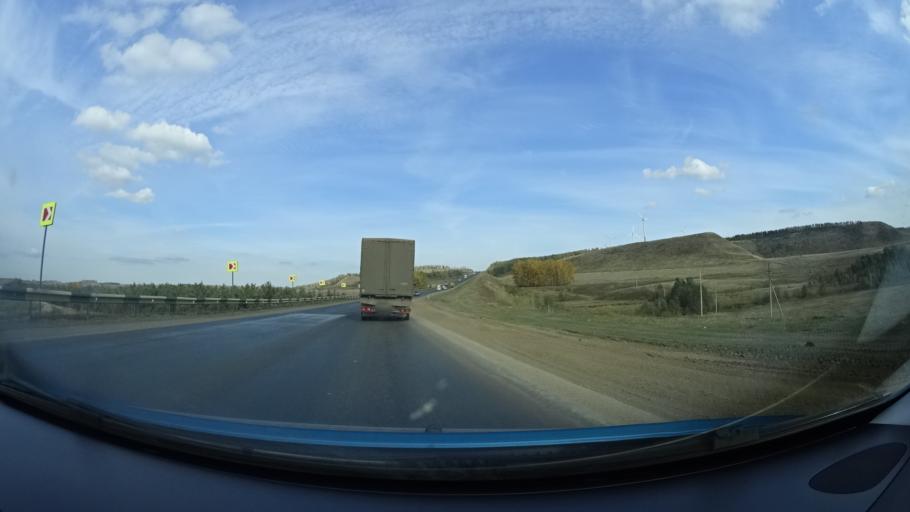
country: RU
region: Bashkortostan
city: Kandry
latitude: 54.5768
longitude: 54.2320
